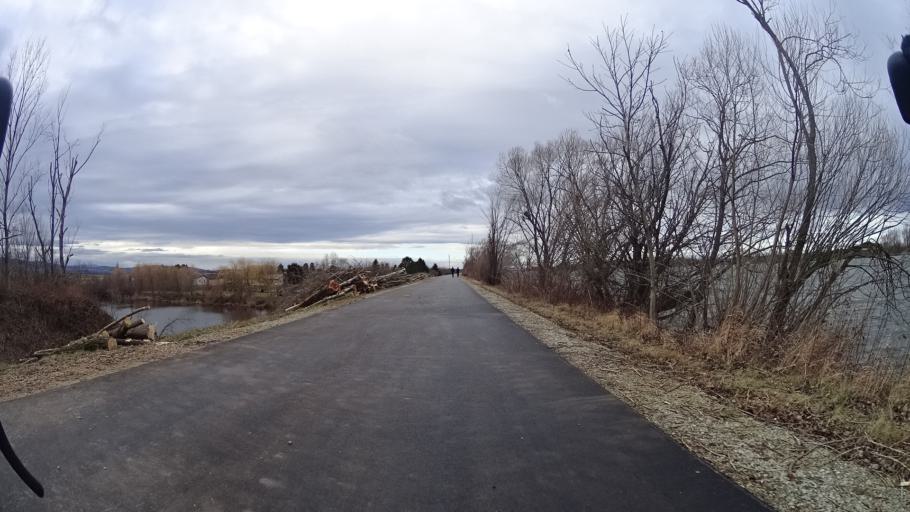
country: AT
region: Lower Austria
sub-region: Politischer Bezirk Tulln
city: Konigstetten
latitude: 48.3351
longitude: 16.1345
